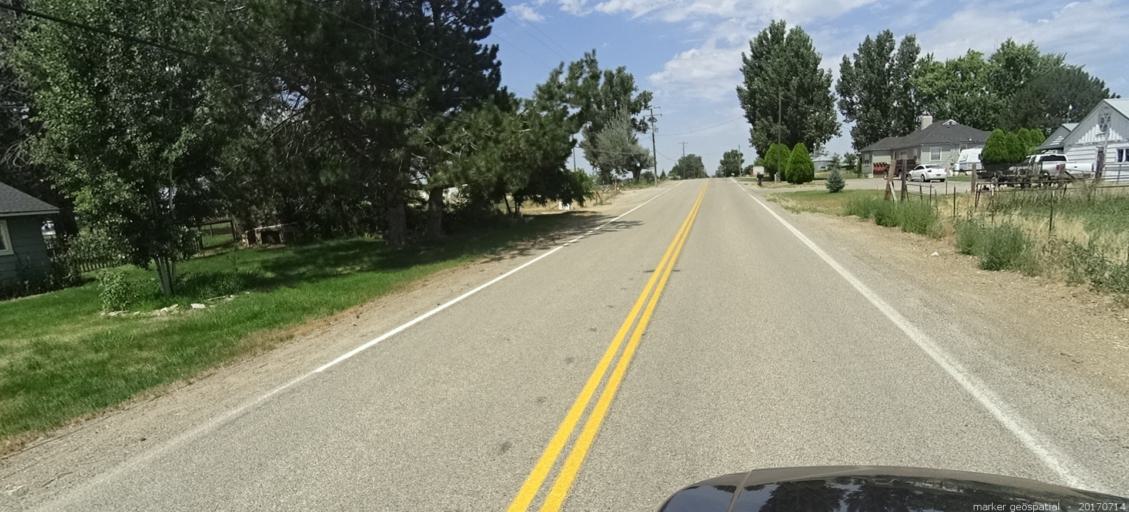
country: US
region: Idaho
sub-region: Ada County
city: Kuna
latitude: 43.5272
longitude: -116.3543
